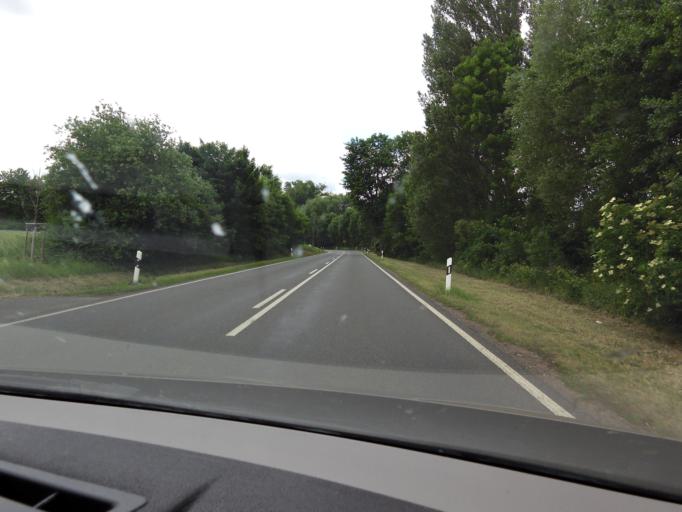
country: DE
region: Thuringia
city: Ernstroda
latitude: 50.8636
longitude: 10.6436
